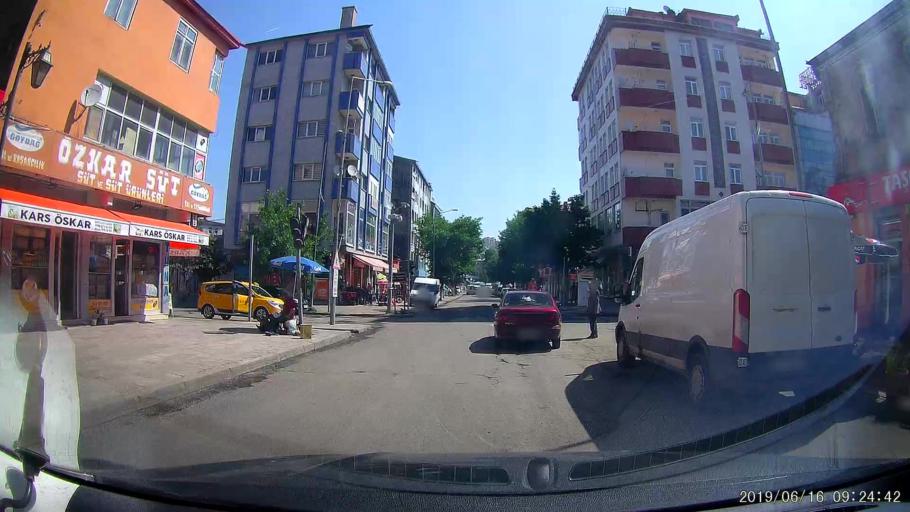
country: TR
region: Kars
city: Kars
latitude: 40.6092
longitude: 43.0941
